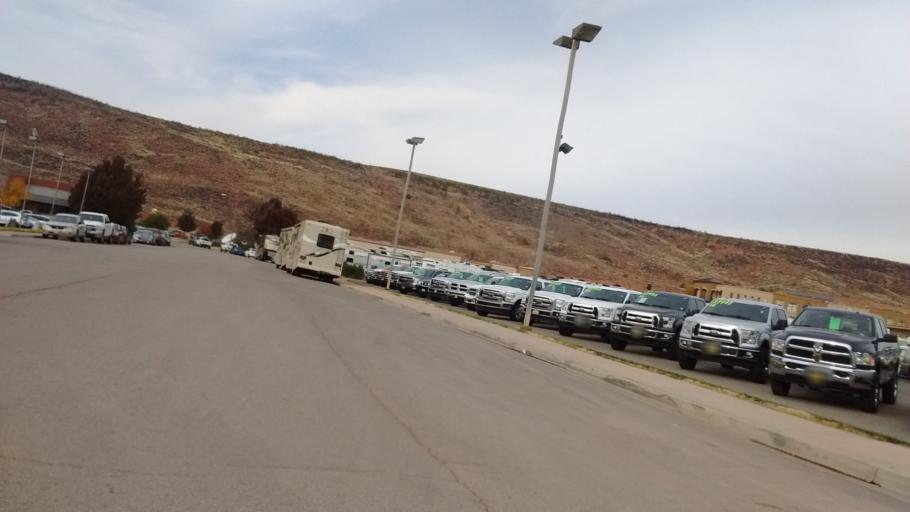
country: US
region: Utah
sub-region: Washington County
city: Saint George
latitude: 37.0807
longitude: -113.5852
